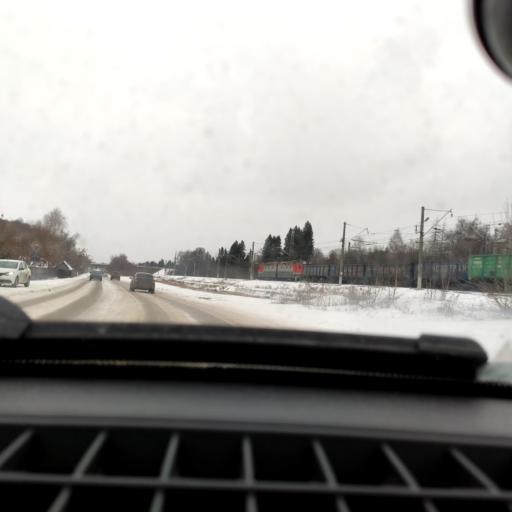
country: RU
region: Bashkortostan
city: Iglino
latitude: 54.8306
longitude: 56.4159
